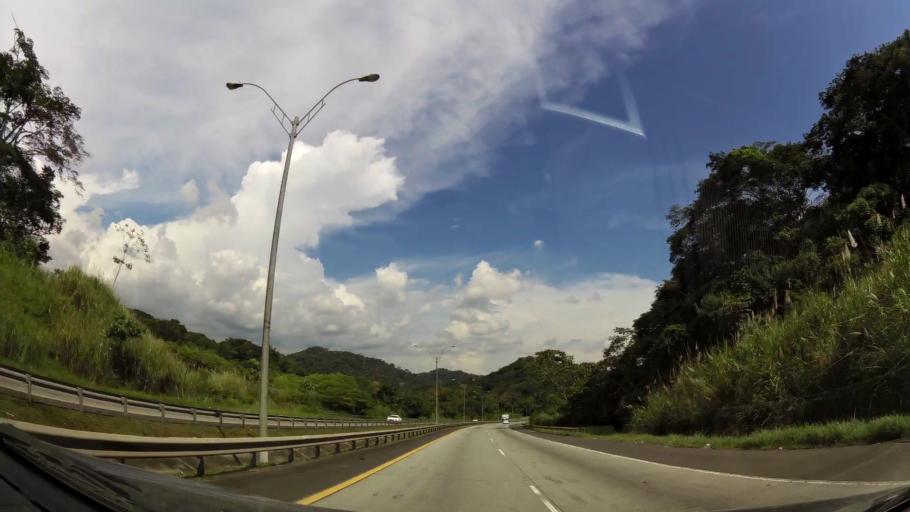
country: PA
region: Panama
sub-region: Distrito de Panama
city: Paraiso
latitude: 9.0371
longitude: -79.6243
